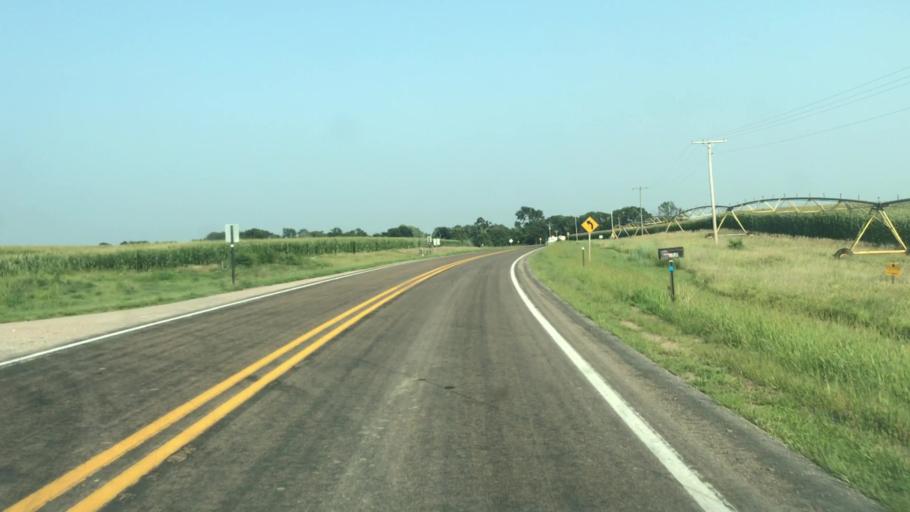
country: US
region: Nebraska
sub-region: Buffalo County
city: Ravenna
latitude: 41.0754
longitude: -98.7287
